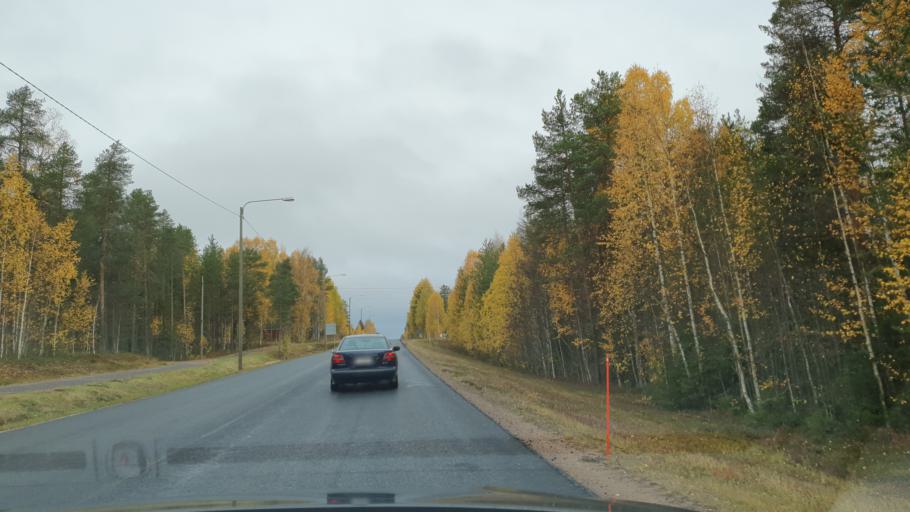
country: FI
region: Lapland
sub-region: Rovaniemi
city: Rovaniemi
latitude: 66.6506
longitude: 25.4537
